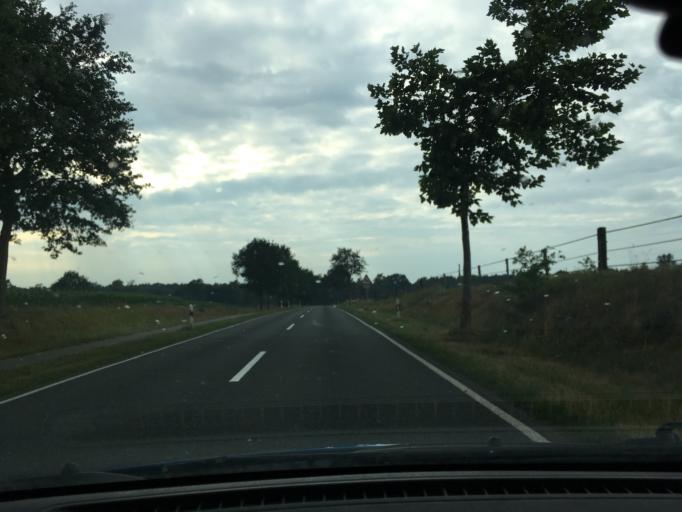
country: DE
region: Lower Saxony
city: Wenzendorf
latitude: 53.3524
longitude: 9.7424
